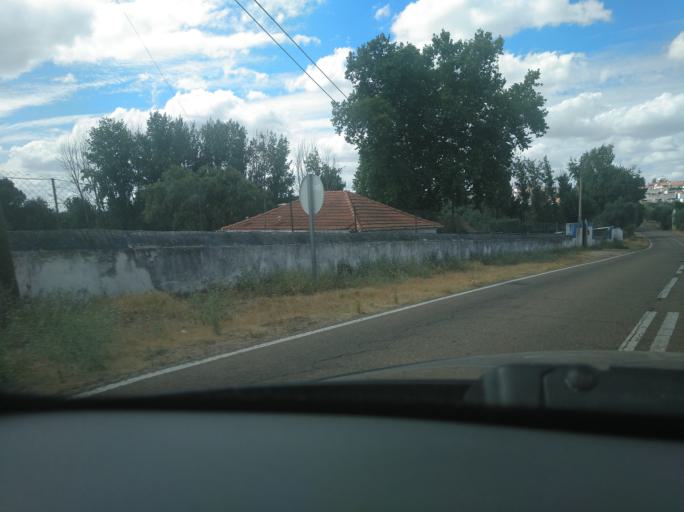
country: PT
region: Portalegre
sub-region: Arronches
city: Arronches
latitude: 39.0475
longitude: -7.4325
